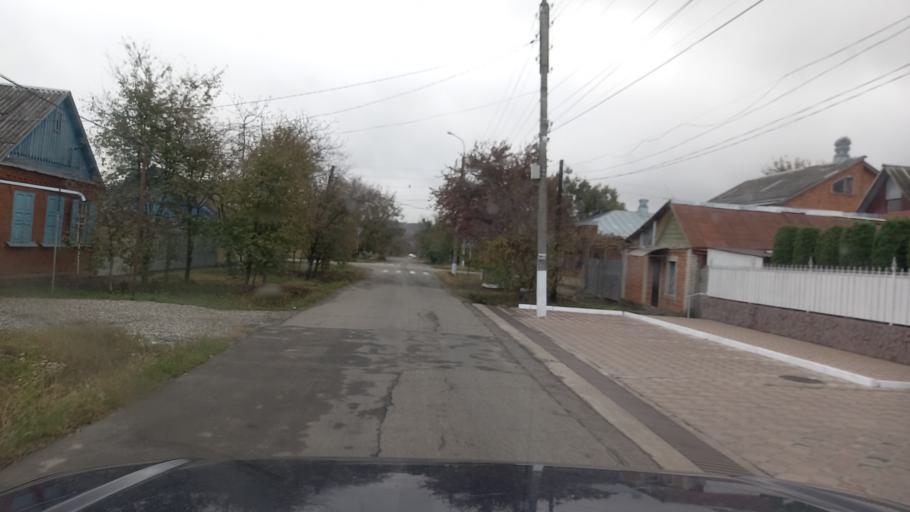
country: RU
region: Adygeya
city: Maykop
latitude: 44.6062
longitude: 40.0842
